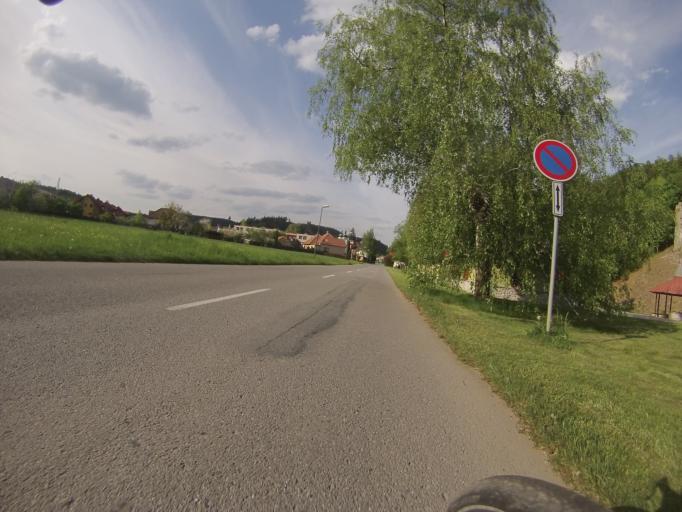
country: CZ
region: South Moravian
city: Ostrov u Macochy
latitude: 49.4109
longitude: 16.7379
